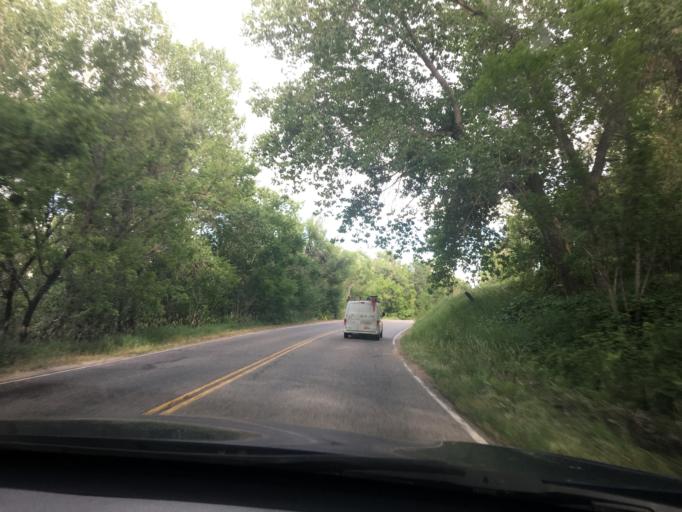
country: US
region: Colorado
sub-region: Jefferson County
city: Applewood
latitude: 39.7666
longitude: -105.1848
